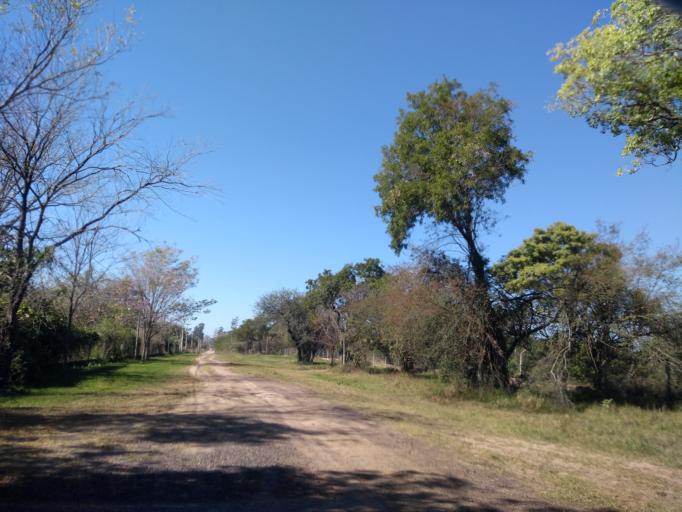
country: AR
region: Chaco
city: Resistencia
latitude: -27.4181
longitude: -58.9520
